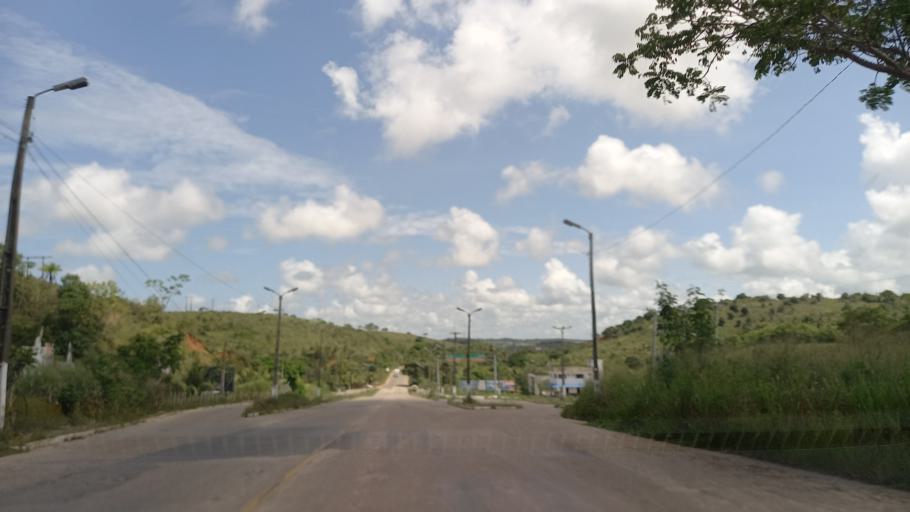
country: BR
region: Pernambuco
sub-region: Barreiros
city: Barreiros
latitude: -8.7892
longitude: -35.1848
